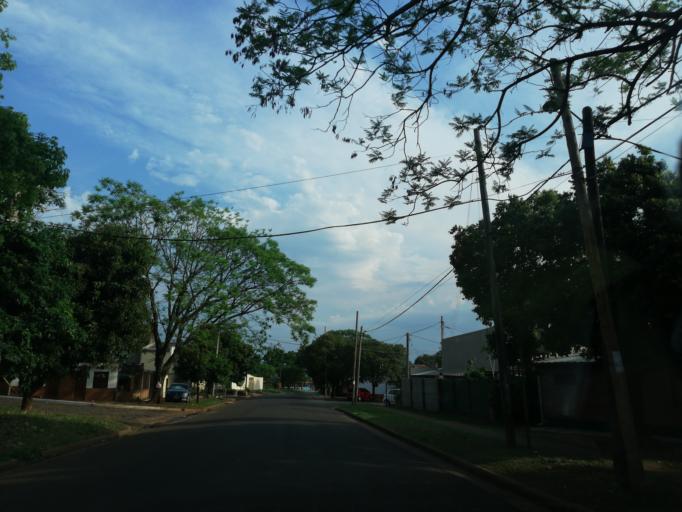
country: AR
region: Misiones
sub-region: Departamento de Capital
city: Posadas
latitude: -27.3695
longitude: -55.9529
